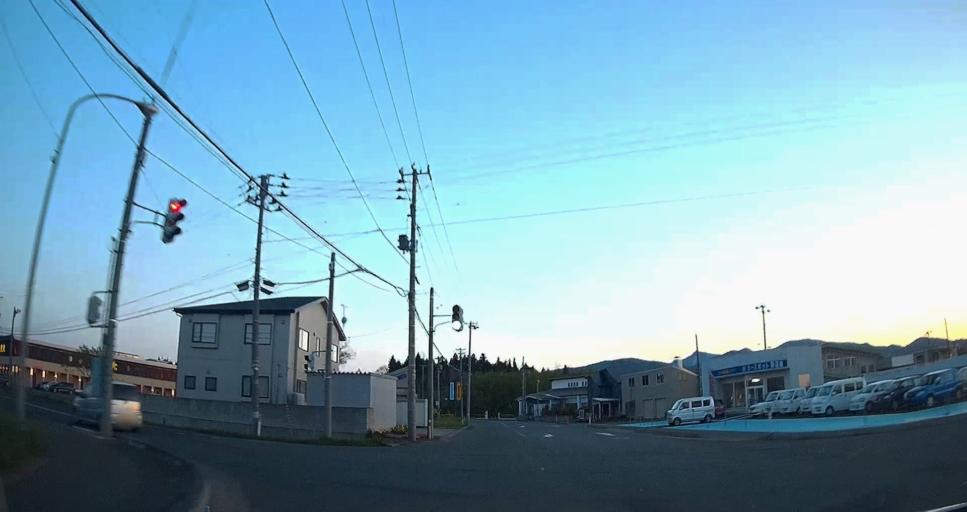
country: JP
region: Aomori
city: Misawa
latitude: 40.8683
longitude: 141.1115
